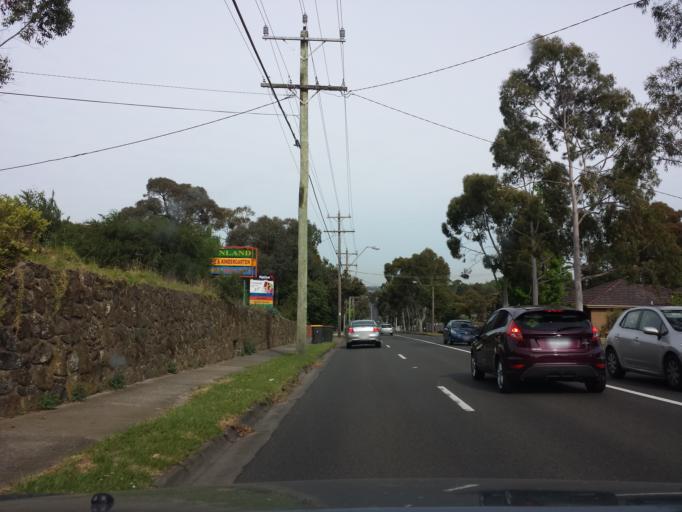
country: AU
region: Victoria
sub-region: Whitehorse
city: Burwood
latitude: -37.8704
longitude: 145.1328
